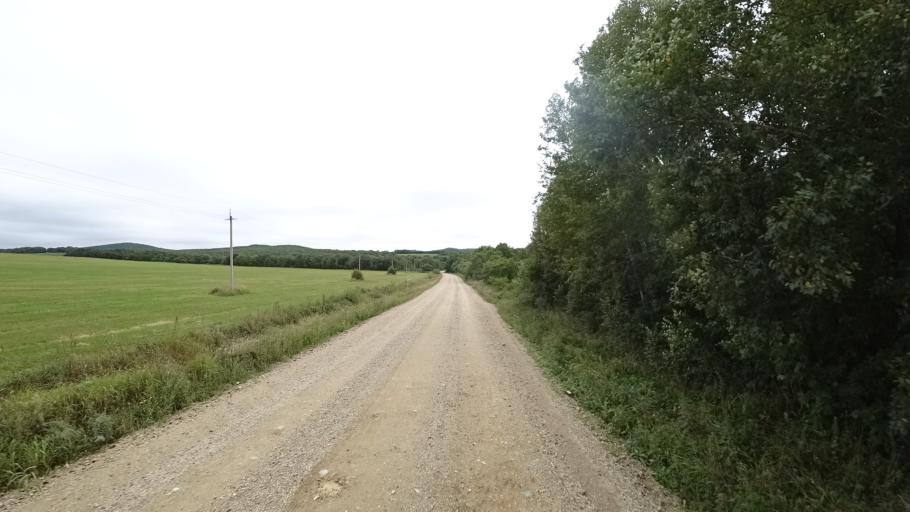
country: RU
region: Primorskiy
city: Lyalichi
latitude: 44.0694
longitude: 132.4771
